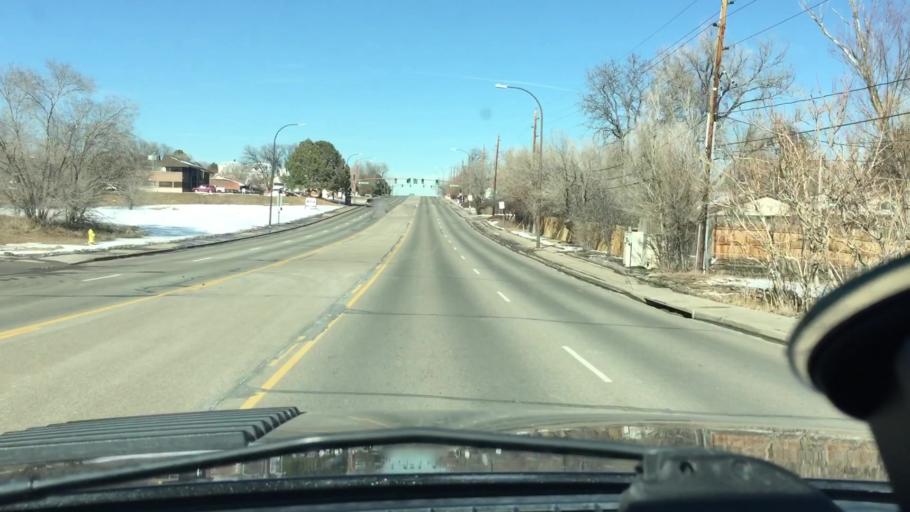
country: US
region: Colorado
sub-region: Adams County
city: Federal Heights
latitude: 39.8511
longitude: -104.9966
